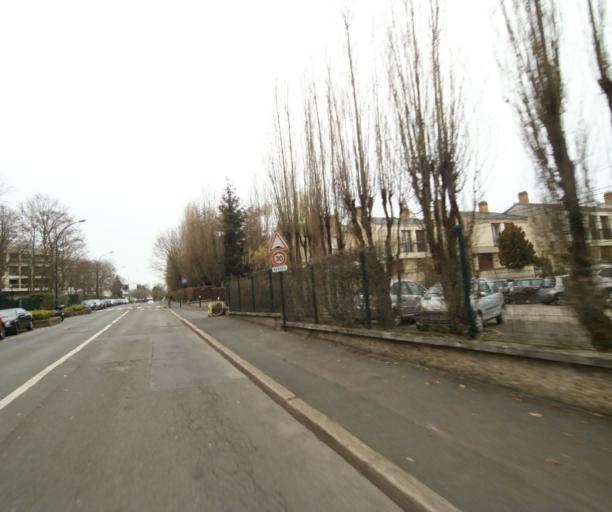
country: FR
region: Ile-de-France
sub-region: Departement des Hauts-de-Seine
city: Saint-Cloud
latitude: 48.8503
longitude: 2.1961
